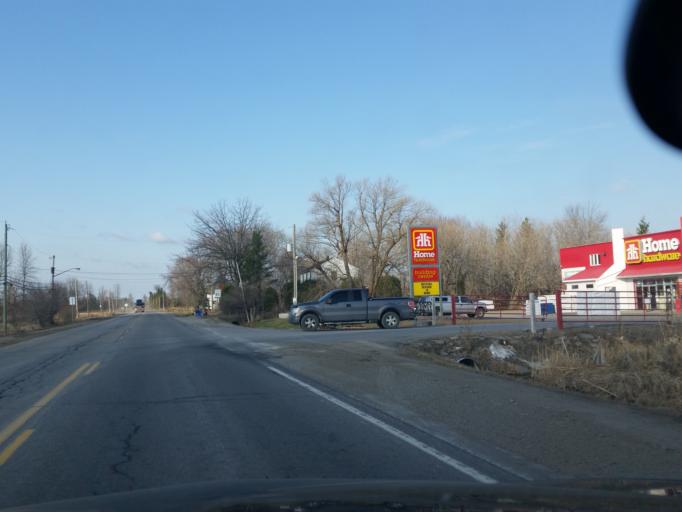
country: CA
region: Ontario
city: Bells Corners
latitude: 45.1873
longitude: -75.8501
